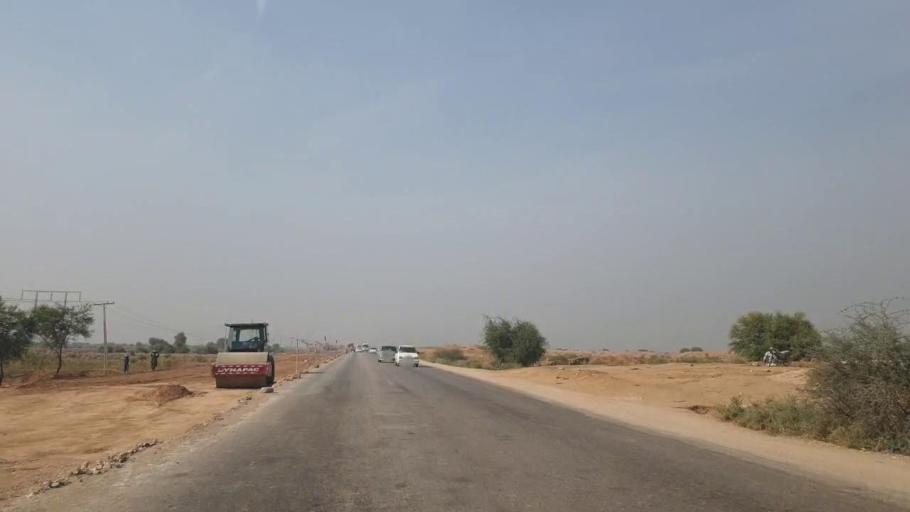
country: PK
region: Sindh
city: Sann
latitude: 26.1229
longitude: 68.0573
